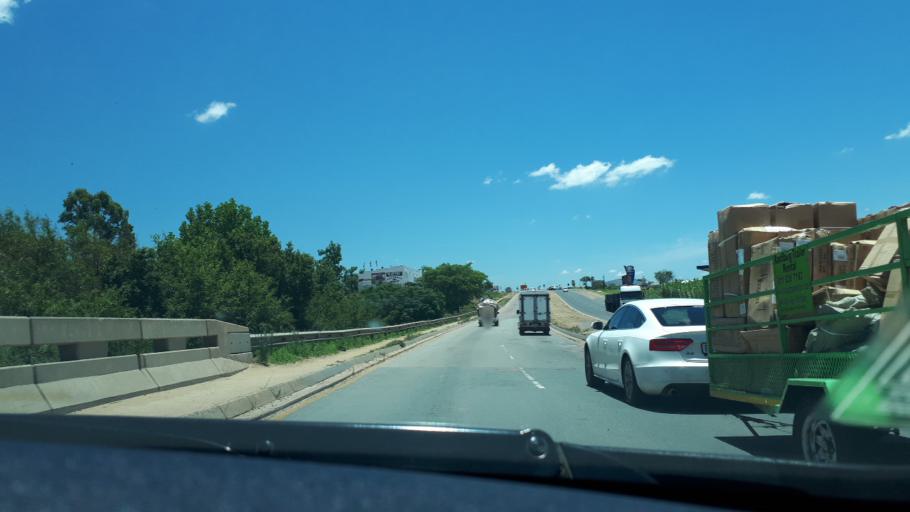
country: ZA
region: Gauteng
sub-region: West Rand District Municipality
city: Muldersdriseloop
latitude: -26.0366
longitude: 27.9479
